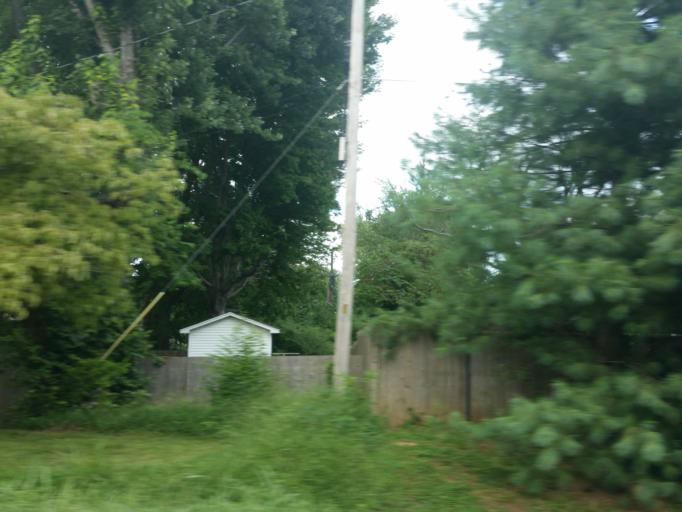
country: US
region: Kentucky
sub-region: Christian County
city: Hopkinsville
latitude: 36.8519
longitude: -87.5159
